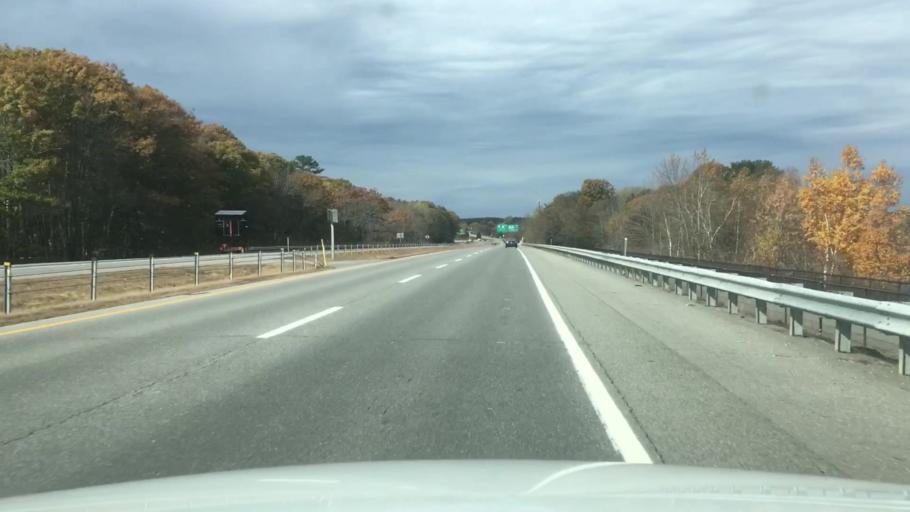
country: US
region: Maine
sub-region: Cumberland County
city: Brunswick
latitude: 43.9149
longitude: -69.9428
